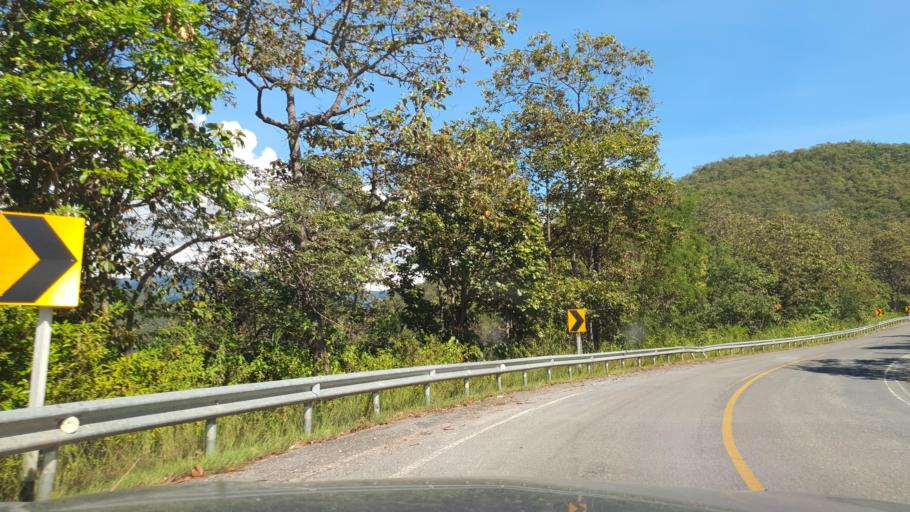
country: TH
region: Chiang Mai
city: Phrao
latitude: 19.3696
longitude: 99.2434
